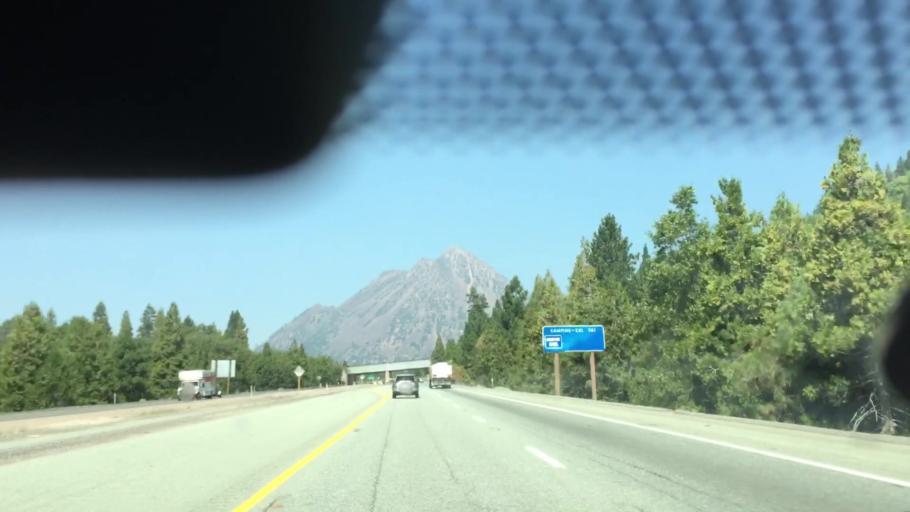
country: US
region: California
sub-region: Siskiyou County
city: Mount Shasta
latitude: 41.3239
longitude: -122.3308
